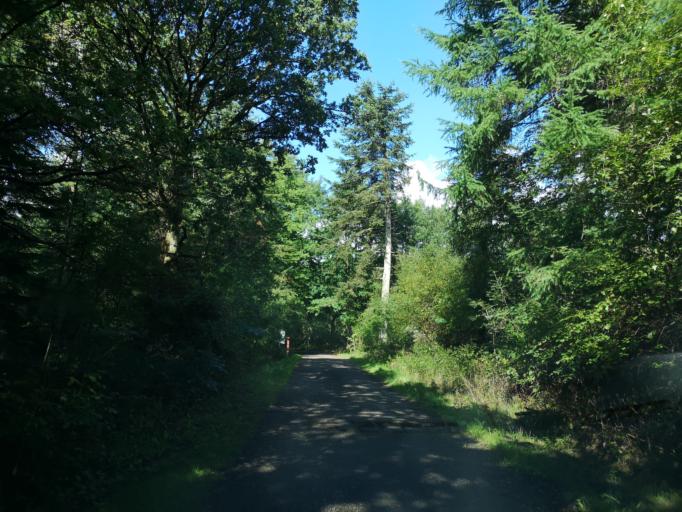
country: DK
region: Central Jutland
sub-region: Holstebro Kommune
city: Holstebro
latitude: 56.3363
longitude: 8.6318
